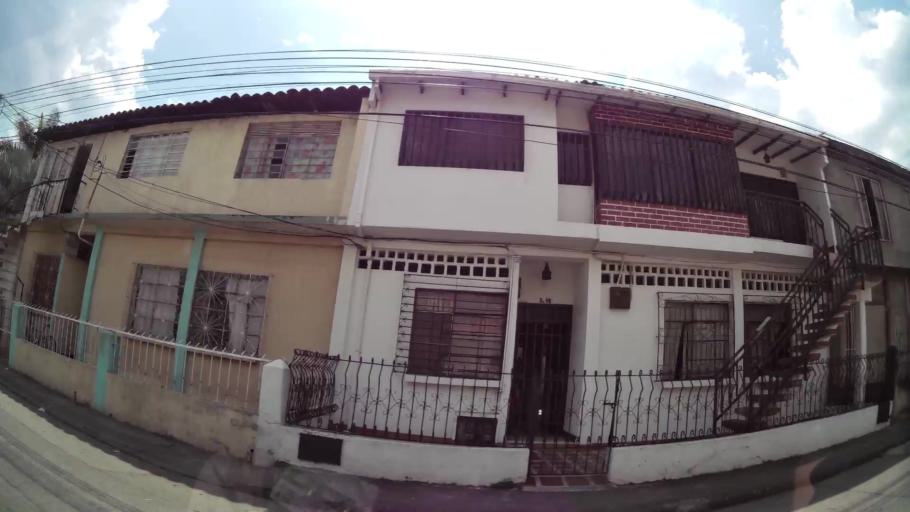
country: CO
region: Valle del Cauca
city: Cali
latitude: 3.4665
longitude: -76.5045
